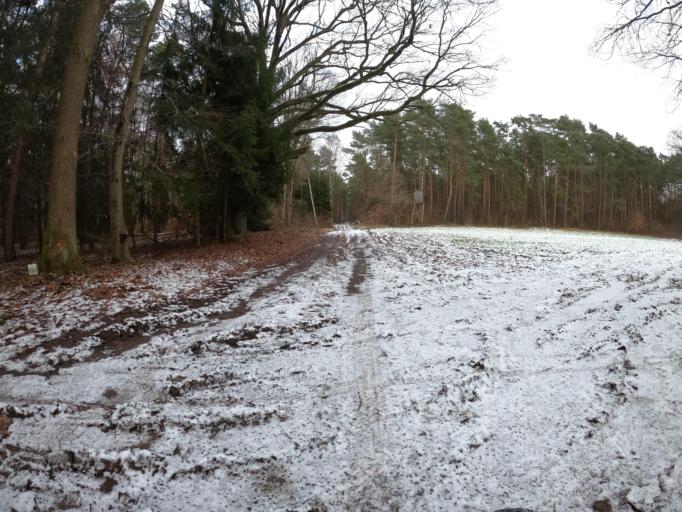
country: PL
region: Lubusz
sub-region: Powiat slubicki
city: Cybinka
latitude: 52.1951
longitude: 14.8681
